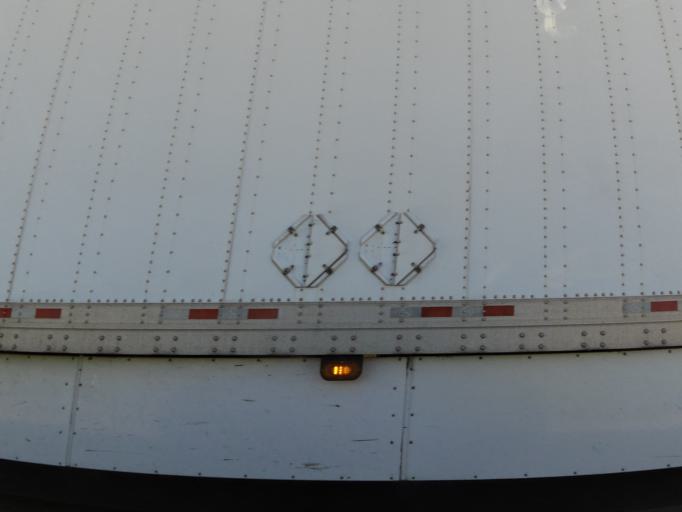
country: US
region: Minnesota
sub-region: Douglas County
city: Alexandria
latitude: 45.9281
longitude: -95.5714
